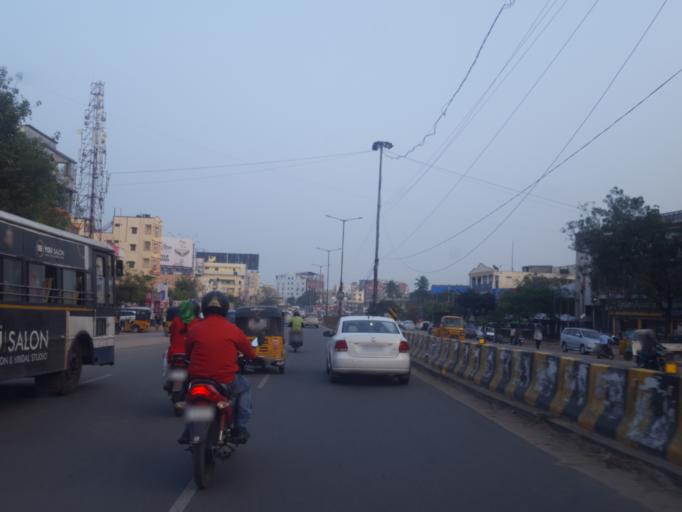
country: IN
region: Telangana
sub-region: Medak
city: Serilingampalle
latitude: 17.5044
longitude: 78.3086
